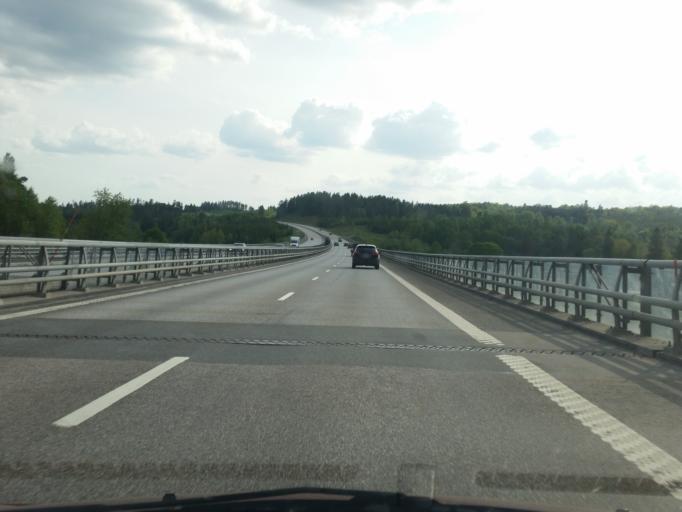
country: SE
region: Vaestra Goetaland
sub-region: Boras Kommun
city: Dalsjofors
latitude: 57.7883
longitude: 13.1292
